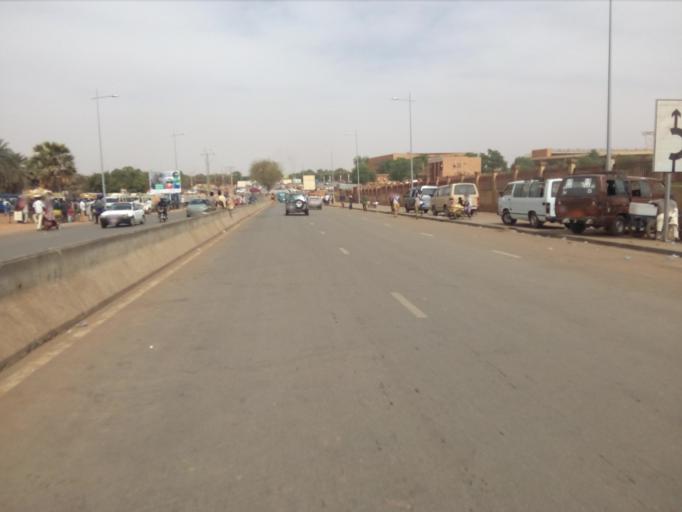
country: NE
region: Niamey
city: Niamey
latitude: 13.5231
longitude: 2.1120
